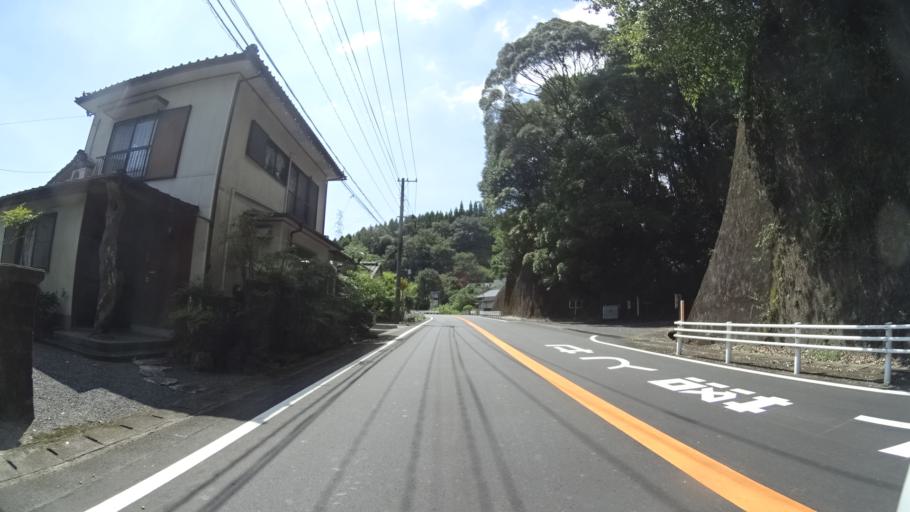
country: JP
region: Kagoshima
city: Kokubu-matsuki
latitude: 31.8501
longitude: 130.7528
